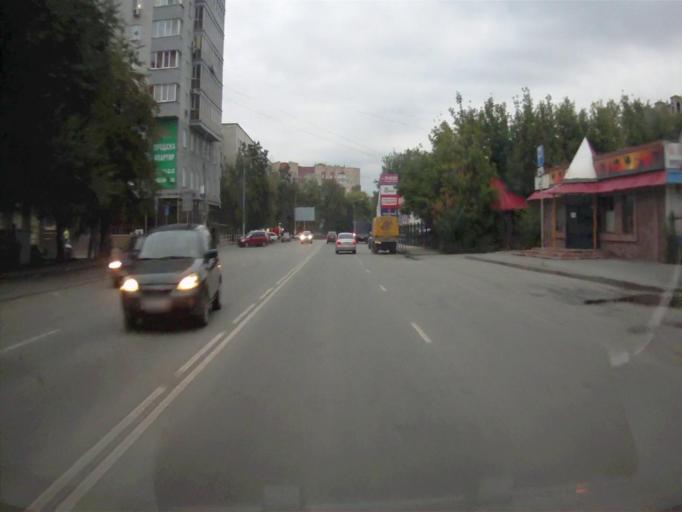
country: RU
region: Chelyabinsk
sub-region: Gorod Chelyabinsk
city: Chelyabinsk
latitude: 55.1522
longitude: 61.3984
